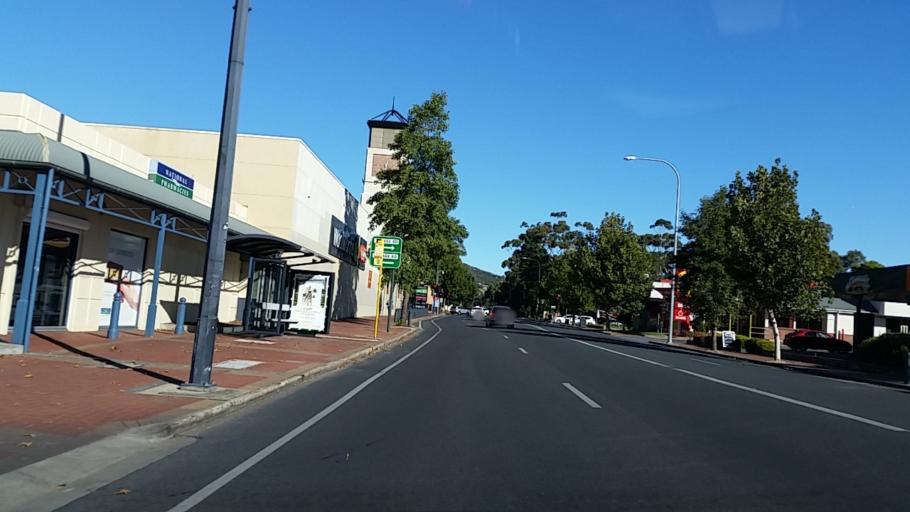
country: AU
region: South Australia
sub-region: Mitcham
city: Hawthorn
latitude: -34.9751
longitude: 138.6094
